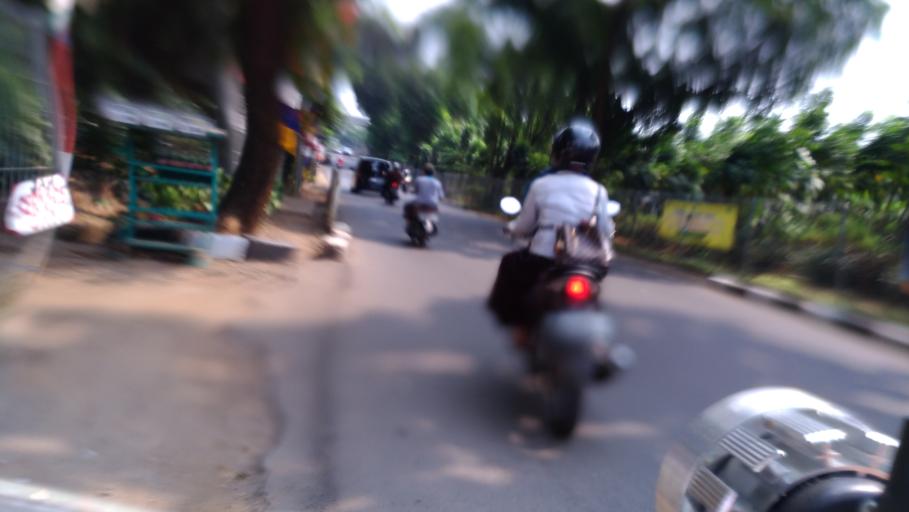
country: ID
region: West Java
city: Cileungsir
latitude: -6.3510
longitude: 106.8930
